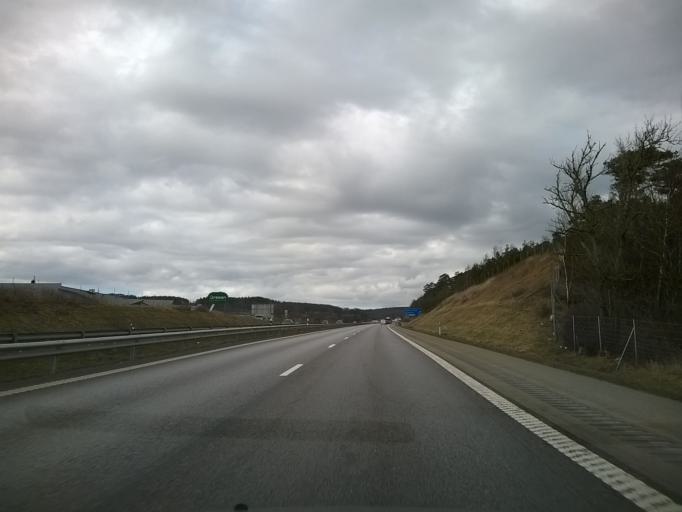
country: SE
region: Halland
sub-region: Varbergs Kommun
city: Varberg
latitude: 57.1637
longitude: 12.2838
